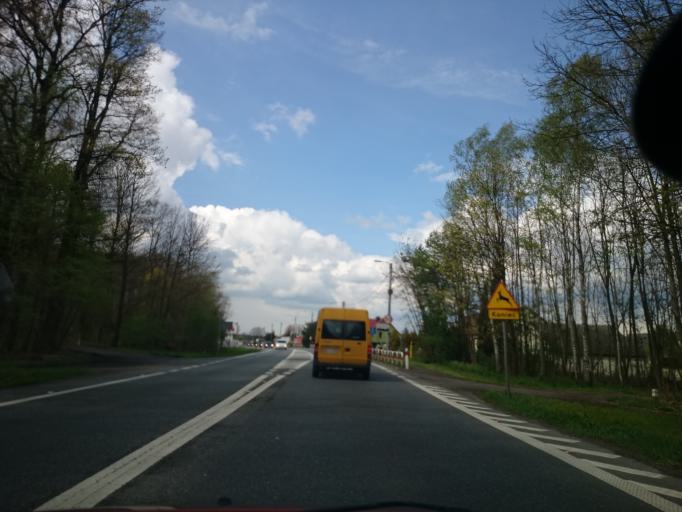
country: PL
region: Opole Voivodeship
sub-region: Powiat opolski
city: Tarnow Opolski
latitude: 50.5989
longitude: 18.0870
